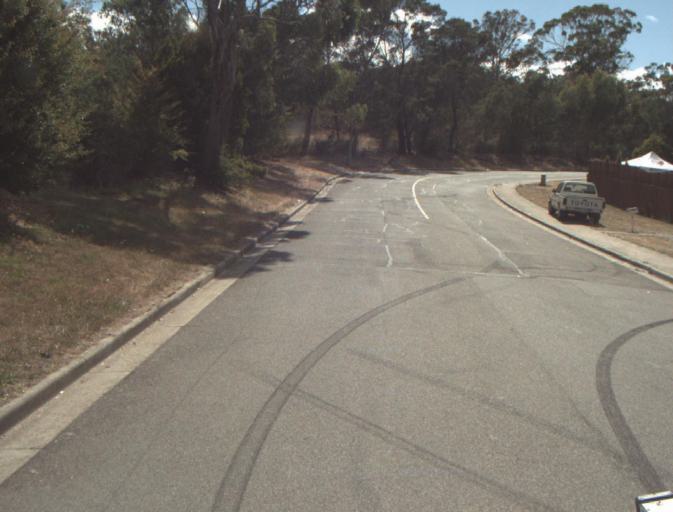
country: AU
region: Tasmania
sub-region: Launceston
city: Newstead
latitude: -41.4157
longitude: 147.1805
